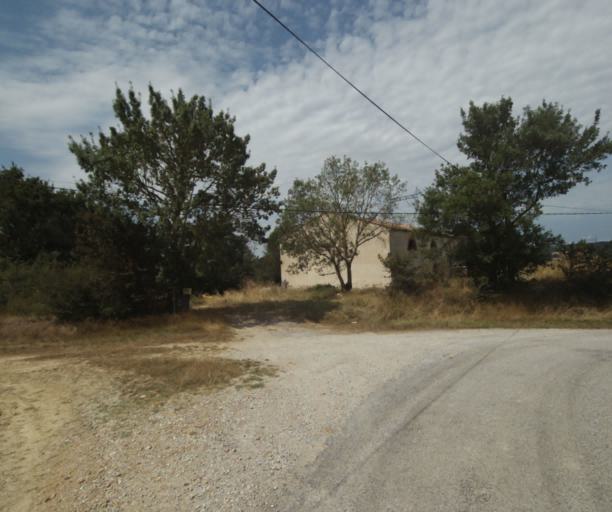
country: FR
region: Midi-Pyrenees
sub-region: Departement de la Haute-Garonne
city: Saint-Felix-Lauragais
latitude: 43.4161
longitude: 1.9067
